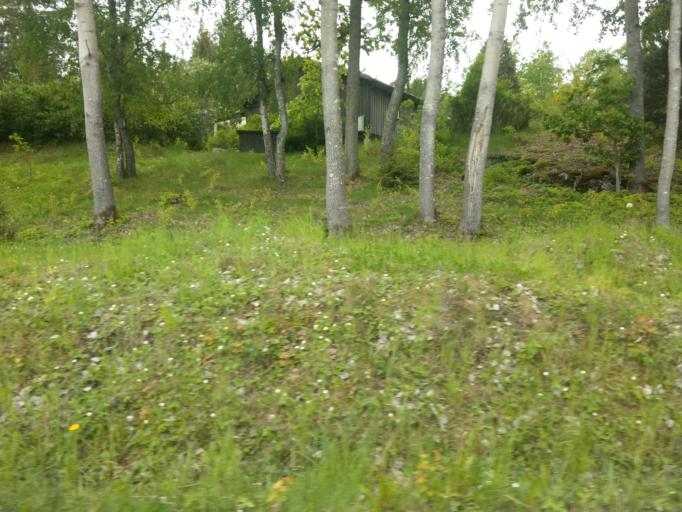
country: SE
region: Stockholm
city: Stenhamra
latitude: 59.4085
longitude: 17.6235
